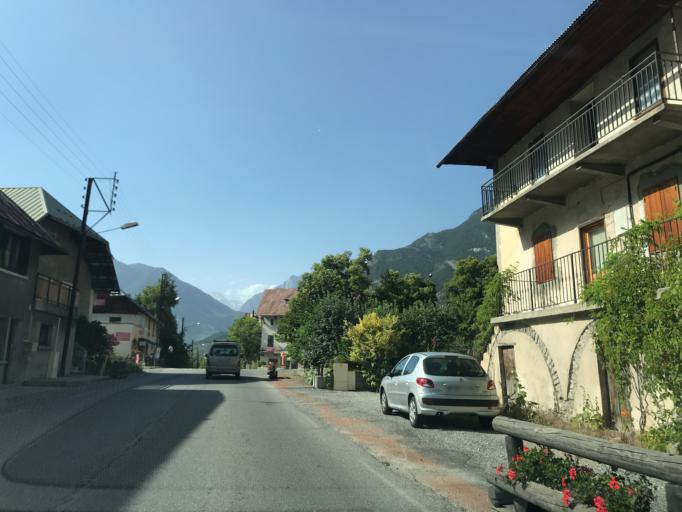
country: FR
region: Provence-Alpes-Cote d'Azur
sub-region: Departement des Hautes-Alpes
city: Saint-Martin-de-Queyrieres
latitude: 44.7497
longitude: 6.5787
